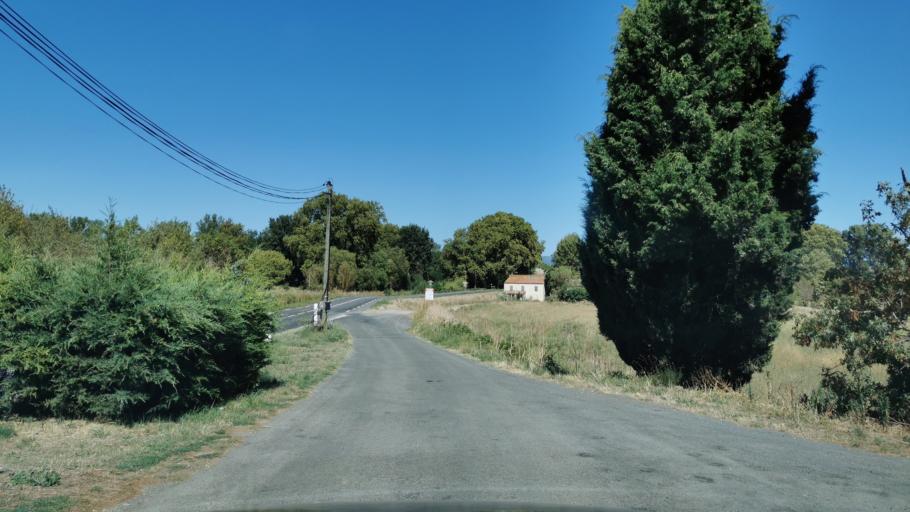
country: FR
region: Languedoc-Roussillon
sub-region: Departement de l'Aude
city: Conques-sur-Orbiel
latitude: 43.2528
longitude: 2.4082
